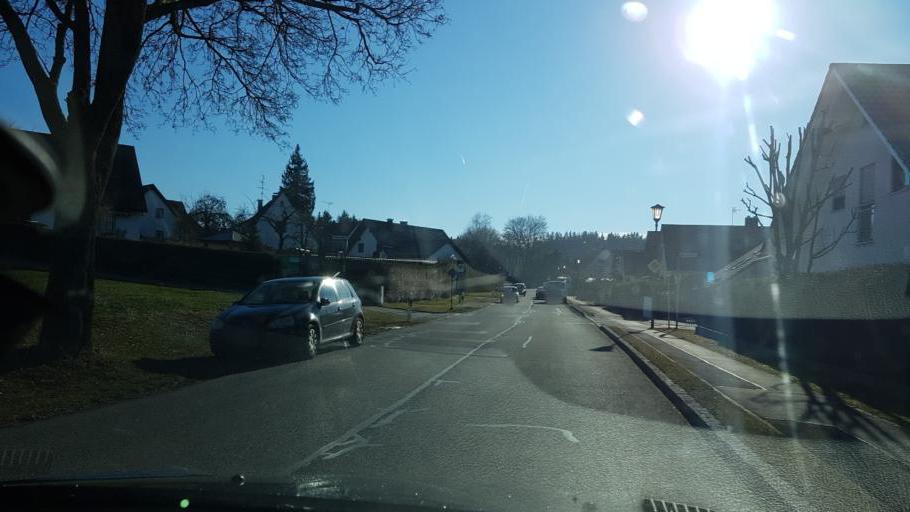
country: DE
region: Bavaria
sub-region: Upper Bavaria
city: Oberschweinbach
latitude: 48.2359
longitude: 11.1591
